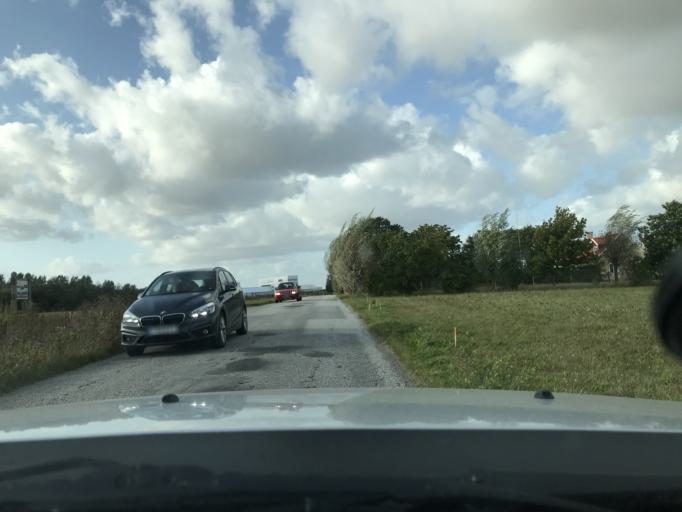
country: SE
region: Skane
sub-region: Lunds Kommun
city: Lund
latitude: 55.7207
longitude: 13.2413
